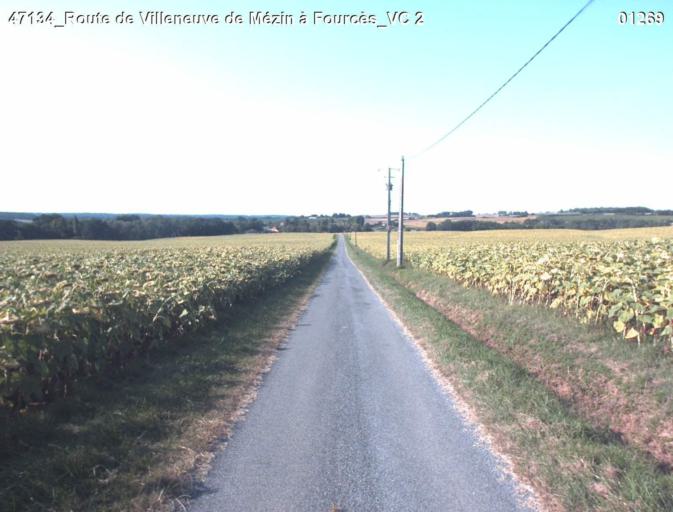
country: FR
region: Aquitaine
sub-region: Departement du Lot-et-Garonne
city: Mezin
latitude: 44.0064
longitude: 0.2487
